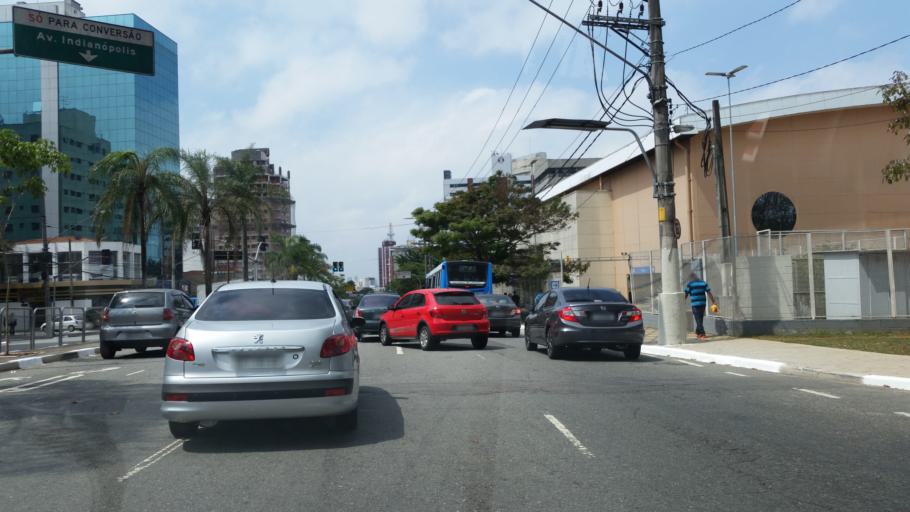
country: BR
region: Sao Paulo
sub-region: Diadema
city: Diadema
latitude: -23.6293
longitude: -46.6457
